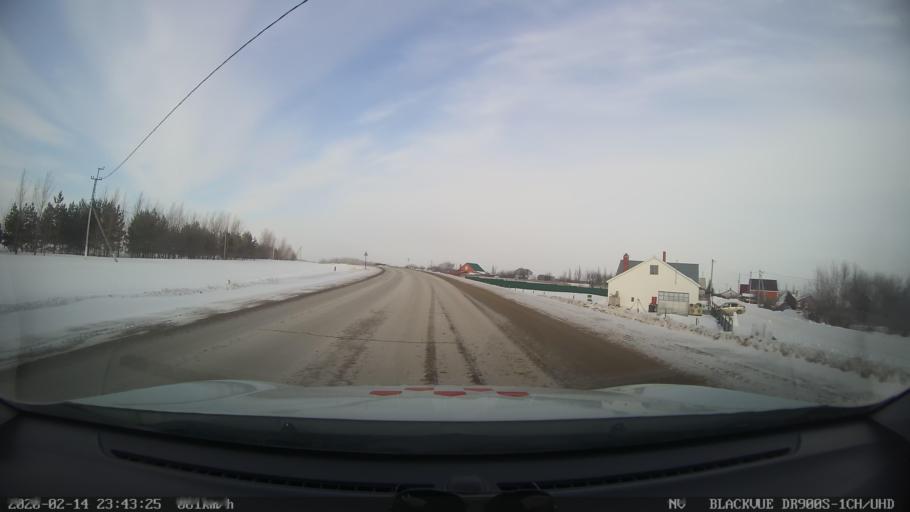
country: RU
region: Tatarstan
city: Kuybyshevskiy Zaton
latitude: 55.2016
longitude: 49.2498
